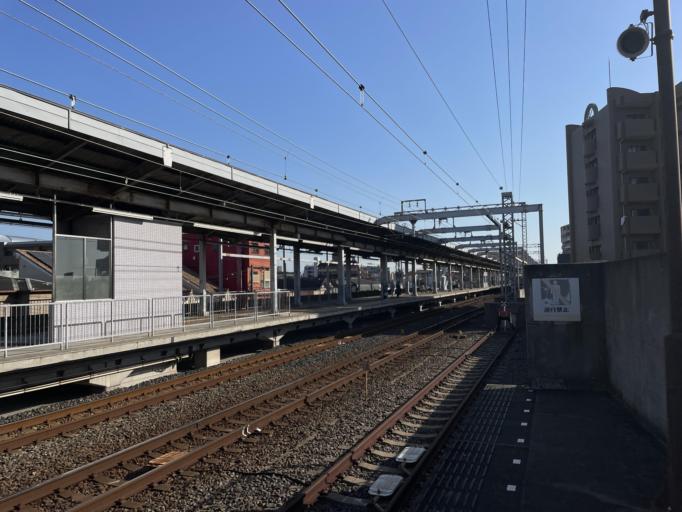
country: JP
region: Osaka
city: Sakai
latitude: 34.6292
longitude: 135.4945
